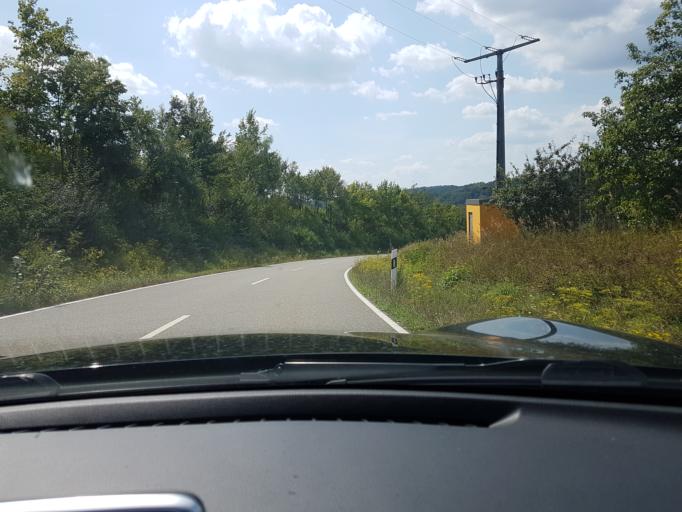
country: DE
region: Baden-Wuerttemberg
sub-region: Karlsruhe Region
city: Limbach
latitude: 49.4233
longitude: 9.2428
